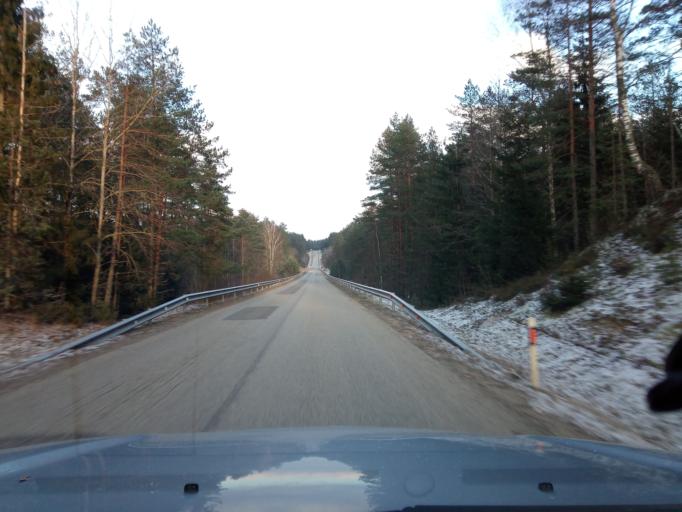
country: LT
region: Alytaus apskritis
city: Varena
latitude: 54.1267
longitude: 24.4574
